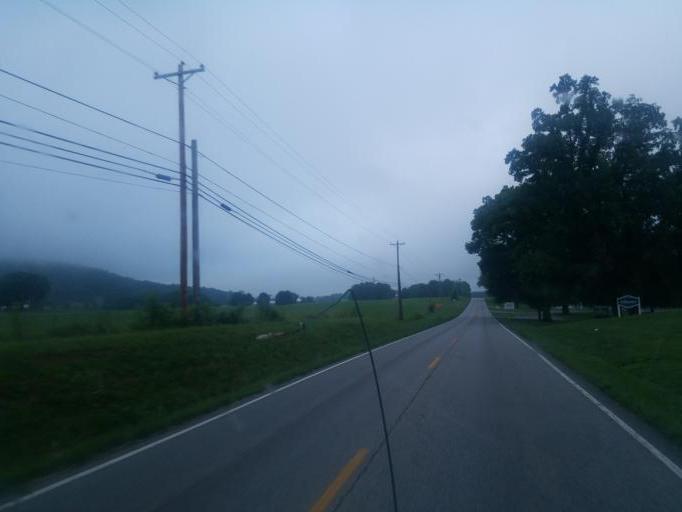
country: US
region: Kentucky
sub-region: Clinton County
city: Albany
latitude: 36.7172
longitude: -85.1351
